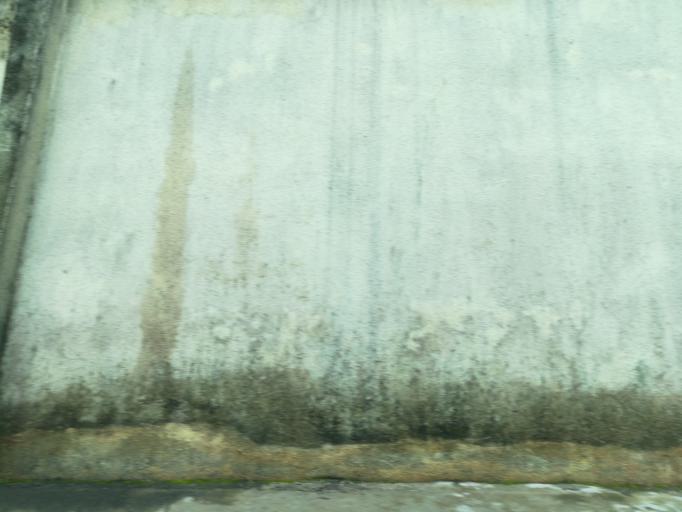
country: NG
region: Rivers
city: Port Harcourt
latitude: 4.8605
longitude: 7.0325
